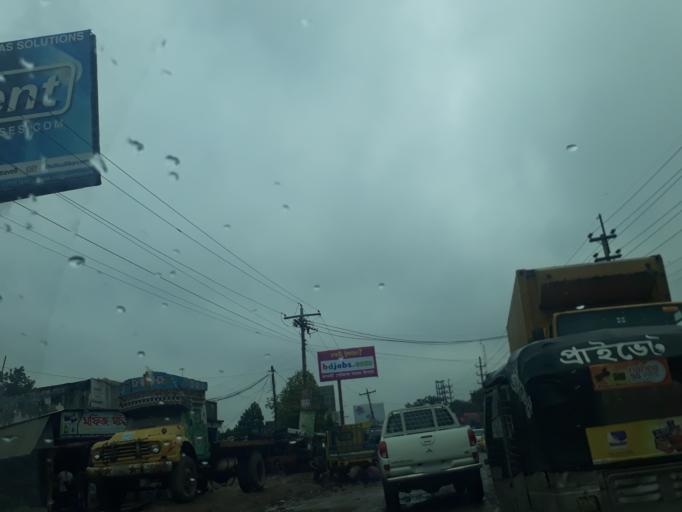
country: BD
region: Dhaka
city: Tungi
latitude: 23.8987
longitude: 90.3295
